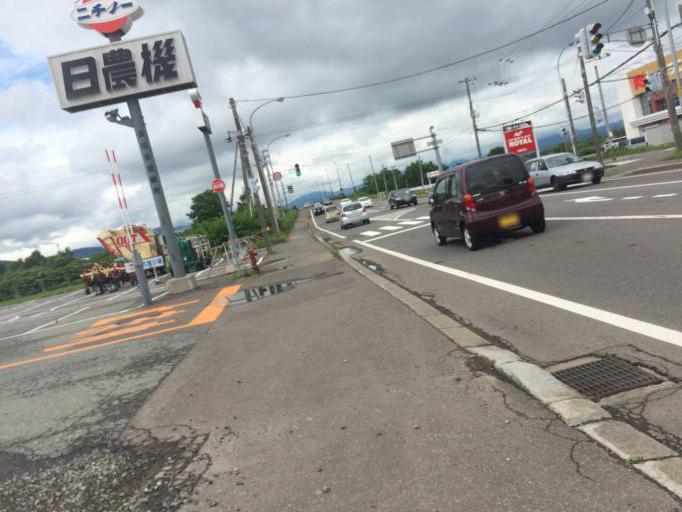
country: JP
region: Hokkaido
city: Niseko Town
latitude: 42.8835
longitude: 140.7509
